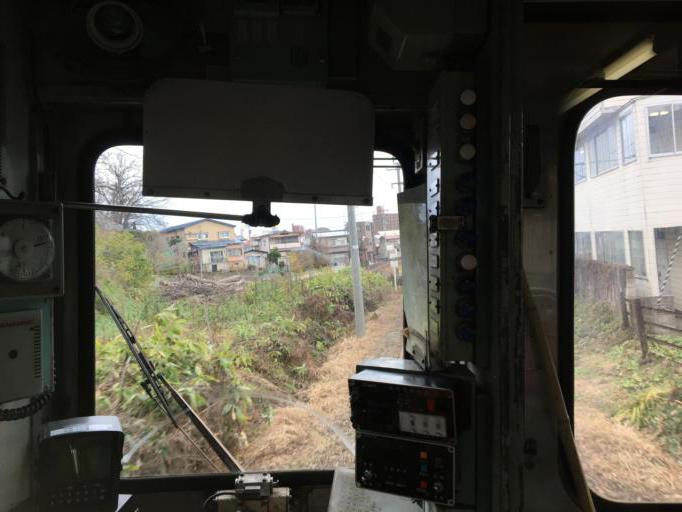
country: JP
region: Aomori
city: Hirosaki
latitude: 40.5952
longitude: 140.4689
